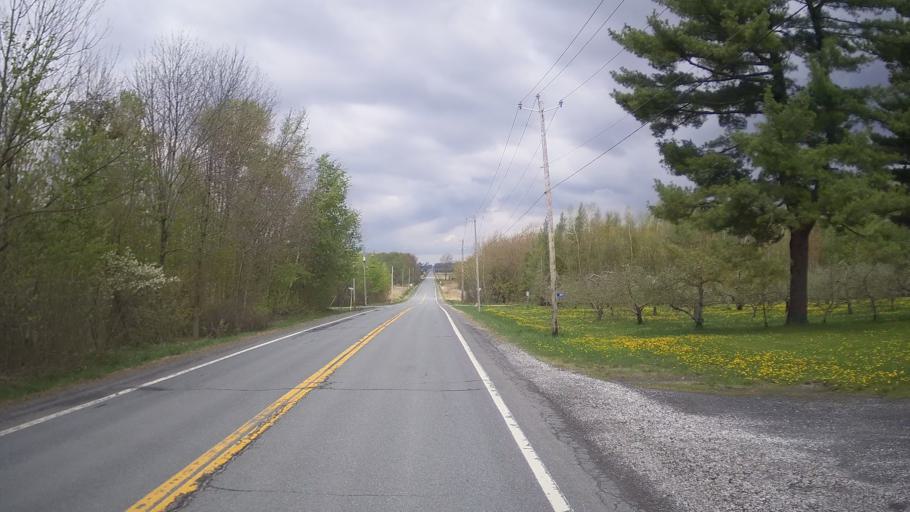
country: CA
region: Quebec
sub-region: Monteregie
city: Farnham
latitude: 45.2482
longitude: -72.8949
